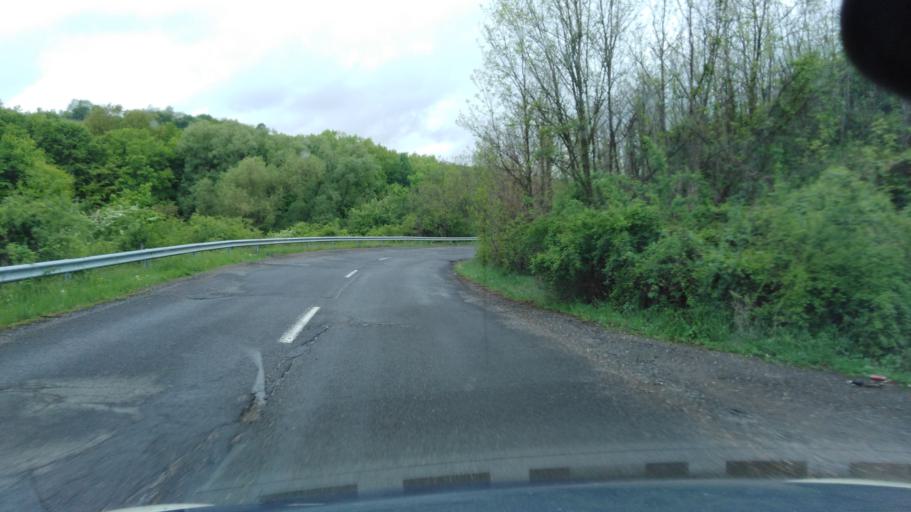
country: HU
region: Nograd
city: Rimoc
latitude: 48.0214
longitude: 19.5925
